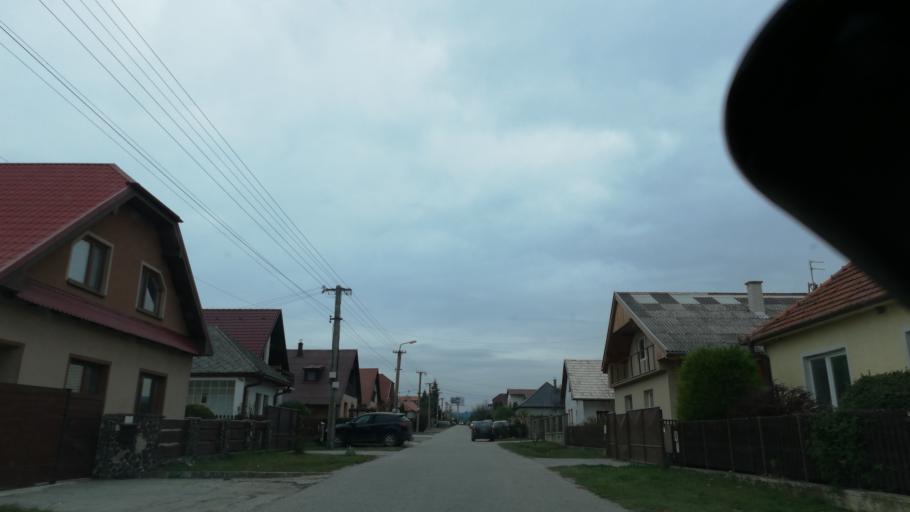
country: SK
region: Nitriansky
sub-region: Okres Nitra
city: Nitra
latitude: 48.3180
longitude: 17.9887
